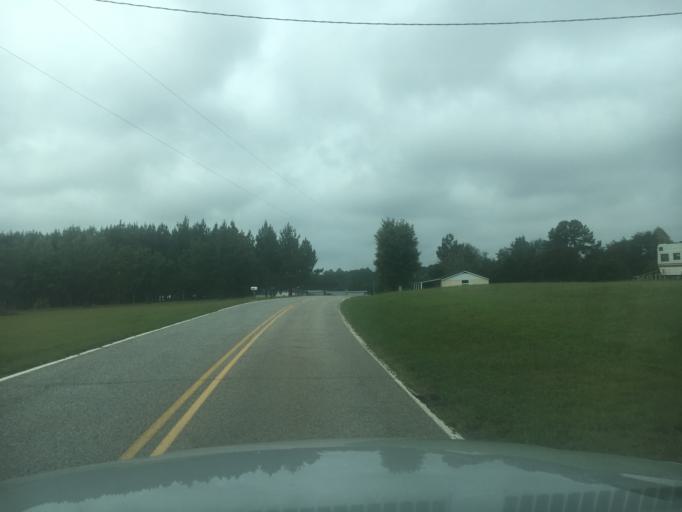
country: US
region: South Carolina
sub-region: Spartanburg County
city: Landrum
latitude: 35.1599
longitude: -82.0949
